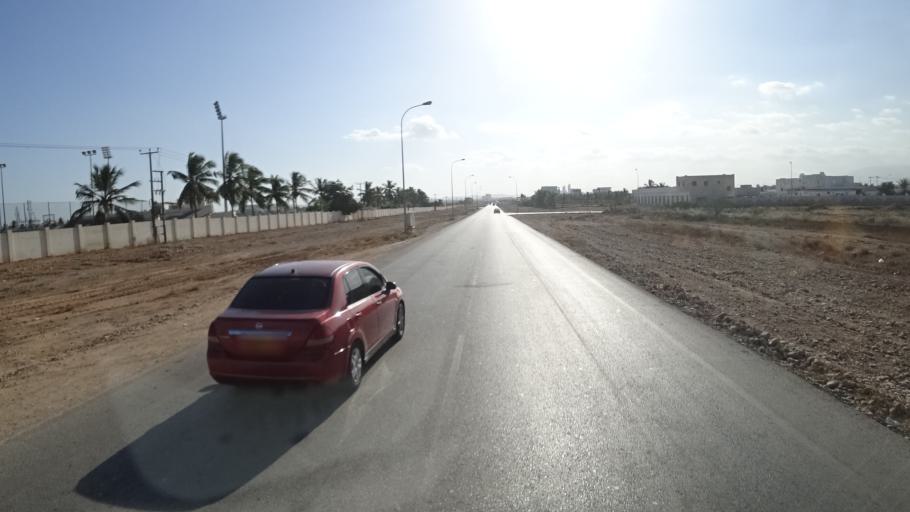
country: OM
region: Zufar
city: Salalah
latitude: 16.9958
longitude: 54.0250
